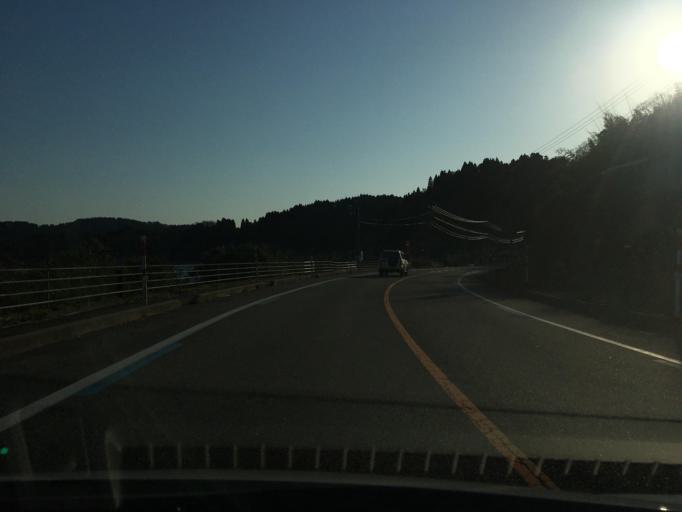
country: JP
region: Toyama
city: Himi
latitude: 36.9434
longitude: 137.0321
